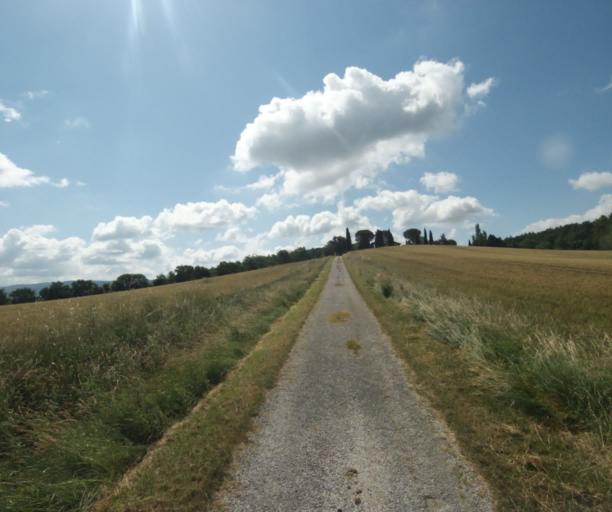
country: FR
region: Midi-Pyrenees
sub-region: Departement de la Haute-Garonne
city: Saint-Felix-Lauragais
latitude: 43.4274
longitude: 1.9305
